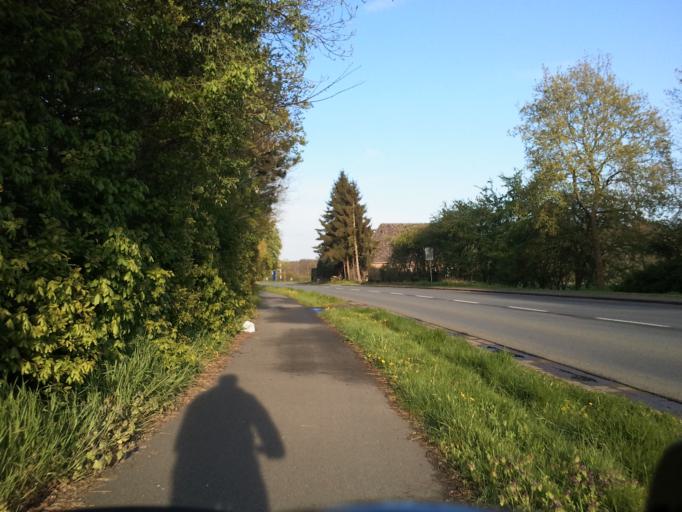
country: DE
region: Lower Saxony
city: Nienburg
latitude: 52.6647
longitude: 9.2519
